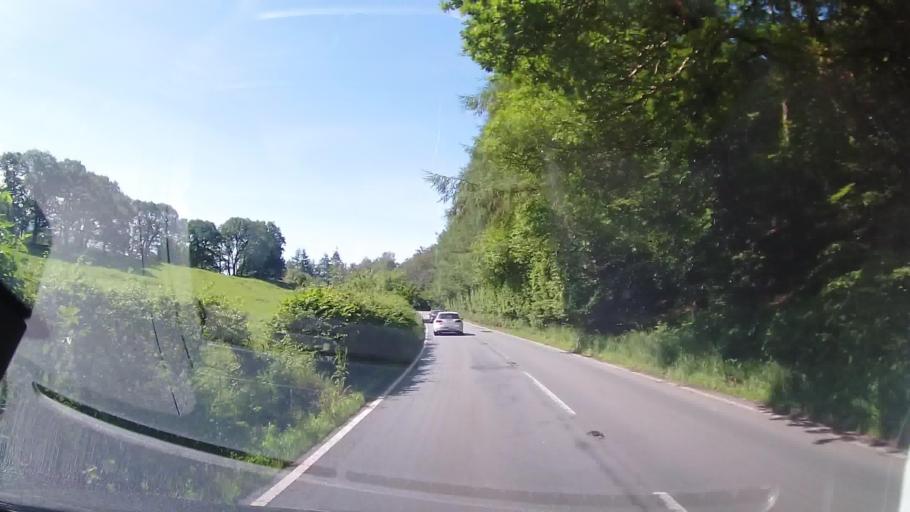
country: GB
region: Wales
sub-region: Sir Powys
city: Machynlleth
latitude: 52.5744
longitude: -3.9507
